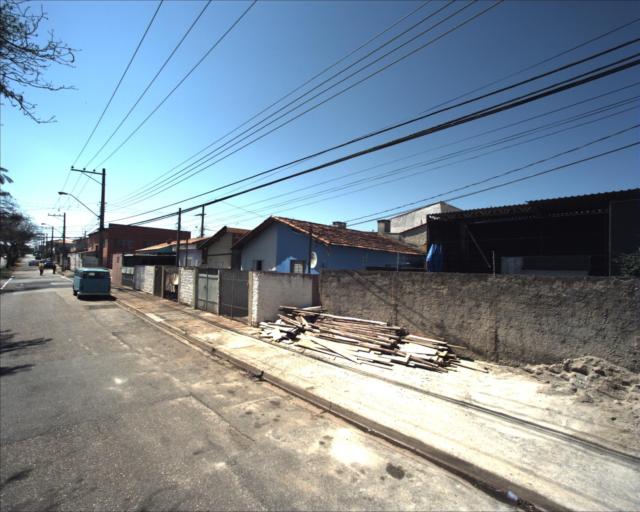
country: BR
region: Sao Paulo
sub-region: Sorocaba
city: Sorocaba
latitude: -23.4714
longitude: -47.4888
